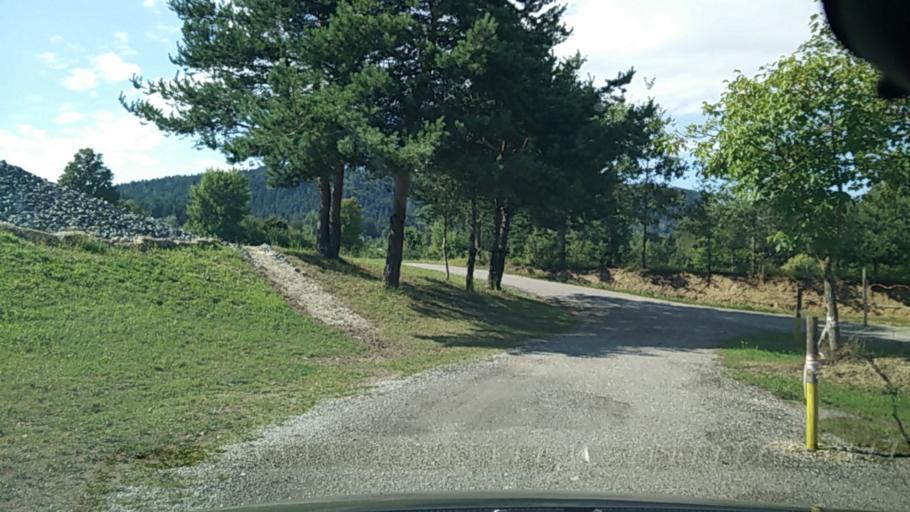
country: AT
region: Carinthia
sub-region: Politischer Bezirk Volkermarkt
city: Sittersdorf
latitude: 46.5833
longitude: 14.5683
